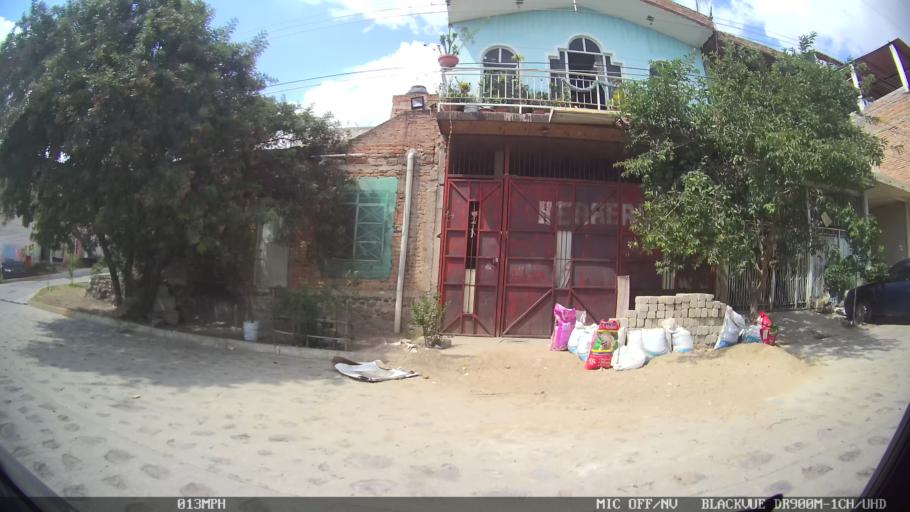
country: MX
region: Jalisco
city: Tlaquepaque
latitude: 20.6829
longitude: -103.2653
